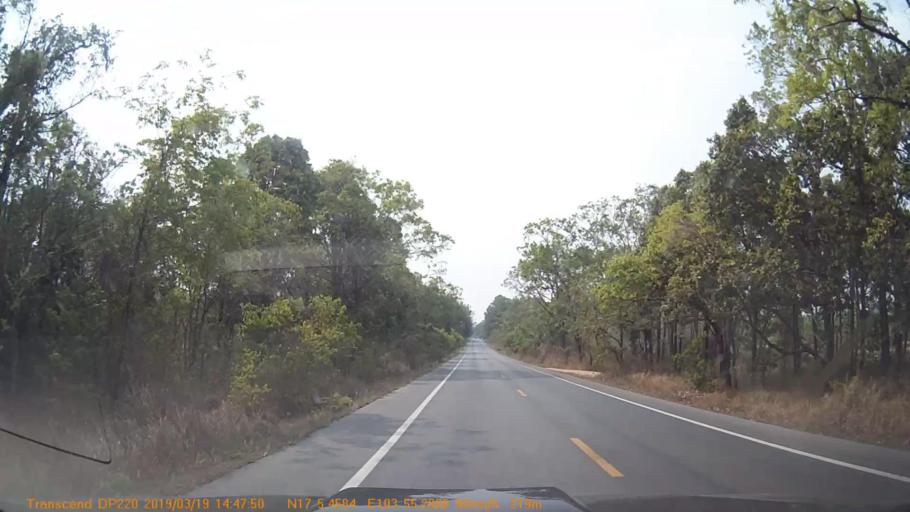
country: TH
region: Sakon Nakhon
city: Kut Bak
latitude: 17.0913
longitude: 103.9211
